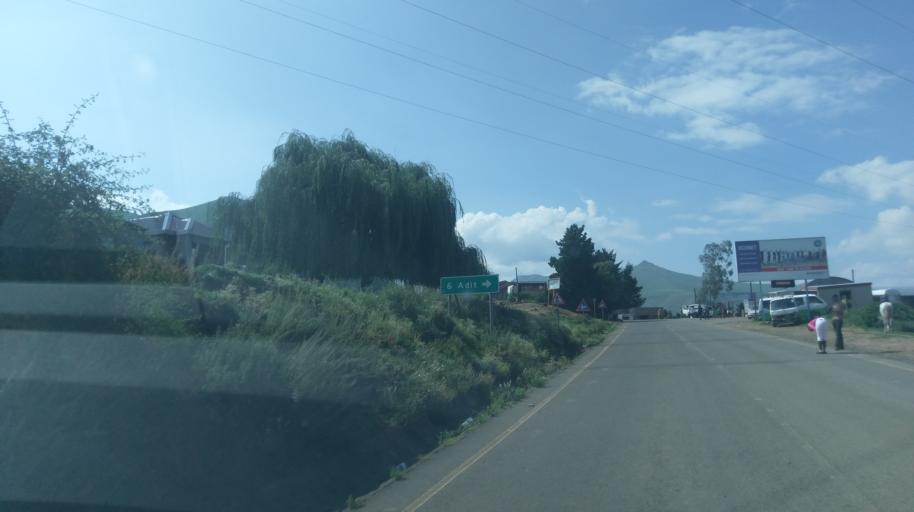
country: LS
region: Butha-Buthe
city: Butha-Buthe
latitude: -29.1099
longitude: 28.4913
